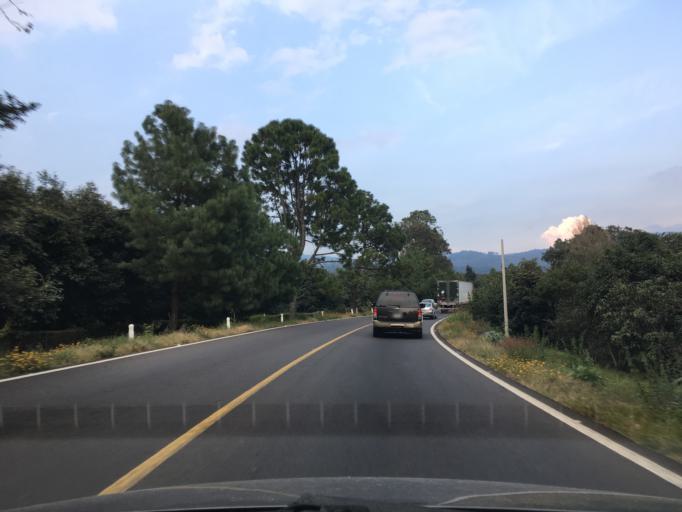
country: MX
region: Michoacan
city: Tingambato
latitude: 19.4972
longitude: -101.8728
